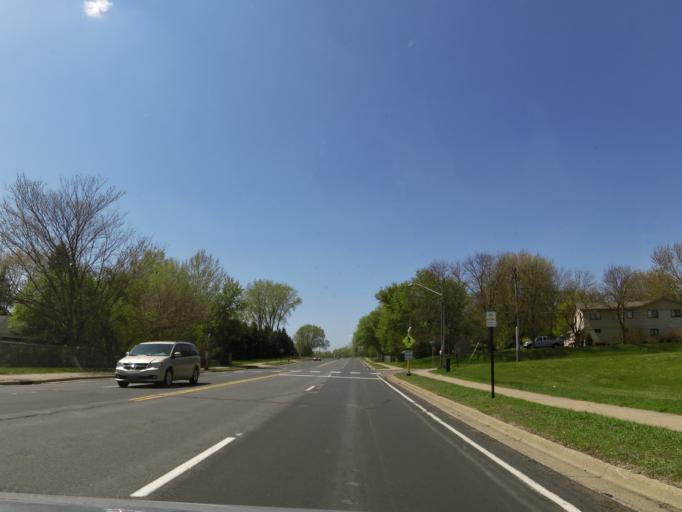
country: US
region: Minnesota
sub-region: Scott County
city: Savage
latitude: 44.7542
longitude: -93.3125
